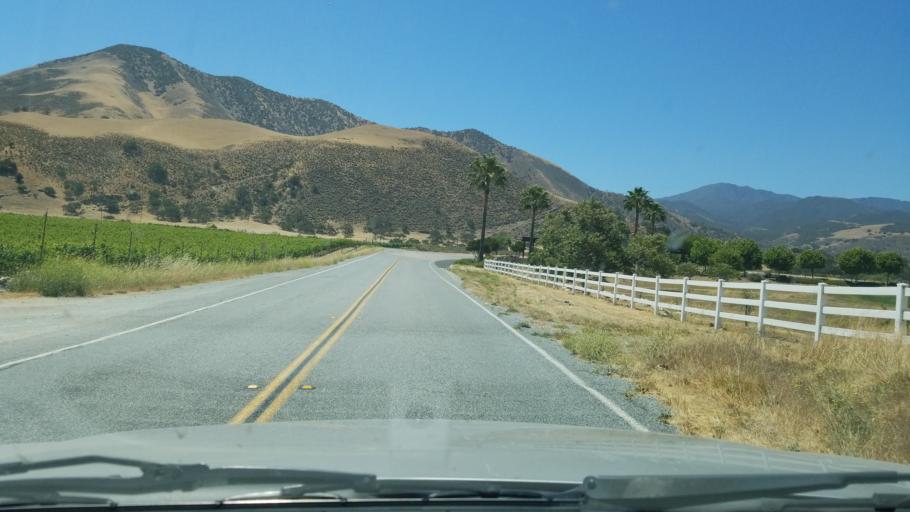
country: US
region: California
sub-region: Monterey County
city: Greenfield
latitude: 36.2840
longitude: -121.3208
